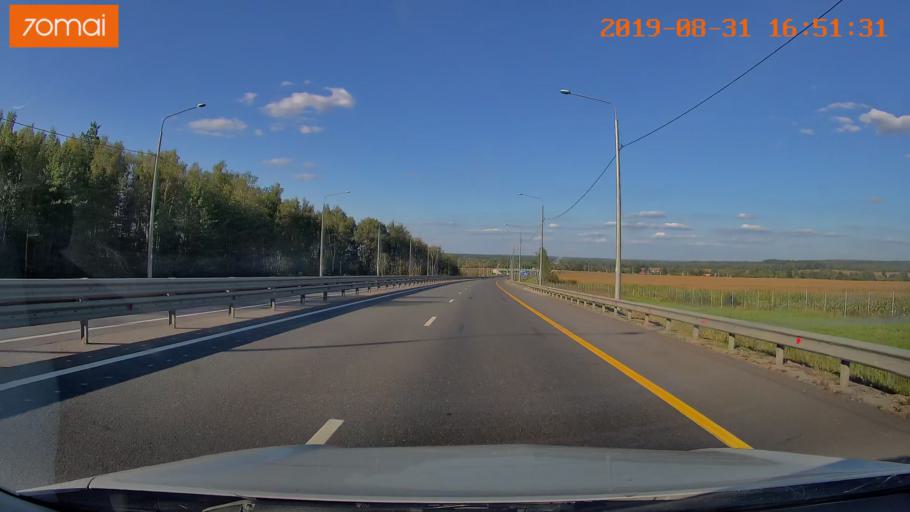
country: RU
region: Kaluga
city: Pyatovskiy
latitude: 54.7277
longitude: 36.1726
